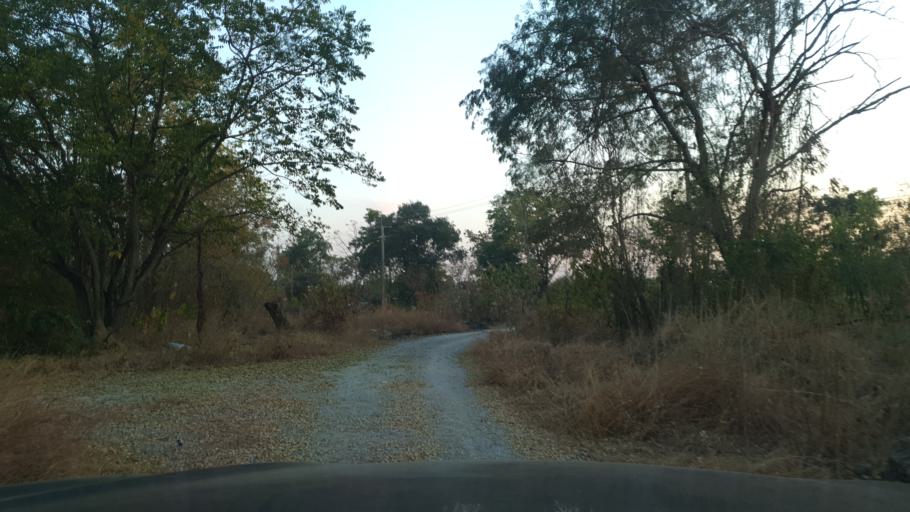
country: TH
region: Nakhon Sawan
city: Kao Liao
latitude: 15.7799
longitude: 99.9770
